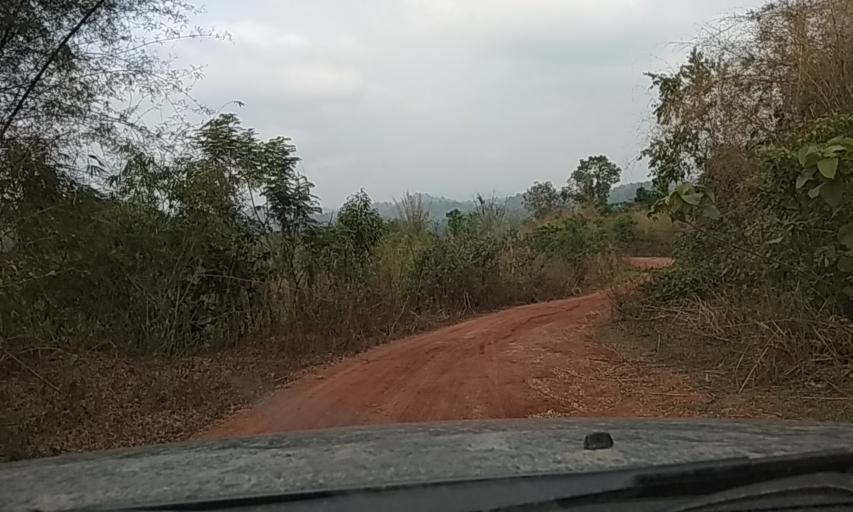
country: TH
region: Nan
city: Mae Charim
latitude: 18.4439
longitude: 101.1893
